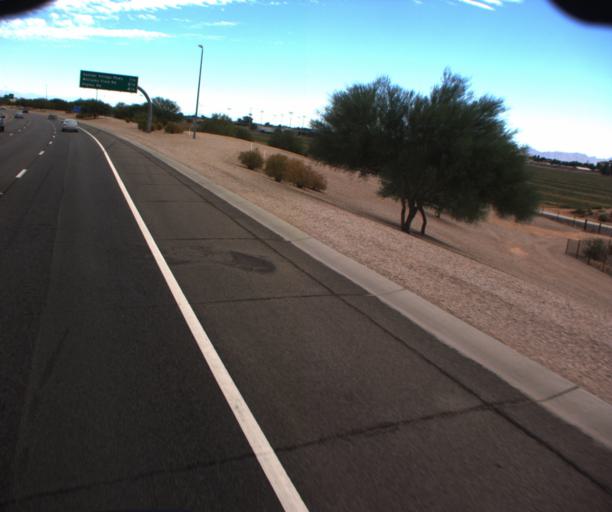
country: US
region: Arizona
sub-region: Maricopa County
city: Gilbert
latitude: 33.2830
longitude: -111.7693
